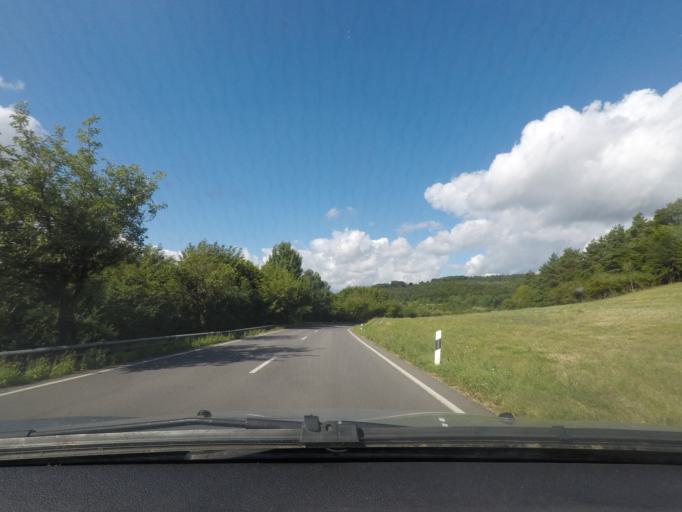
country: LU
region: Grevenmacher
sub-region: Canton de Grevenmacher
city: Junglinster
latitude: 49.7349
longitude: 6.2733
